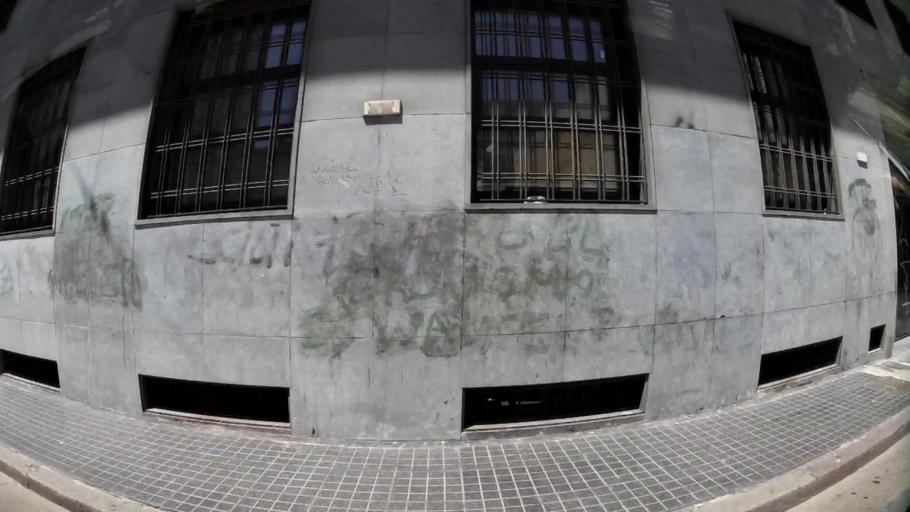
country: AR
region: Buenos Aires F.D.
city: Buenos Aires
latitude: -34.6116
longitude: -58.3769
